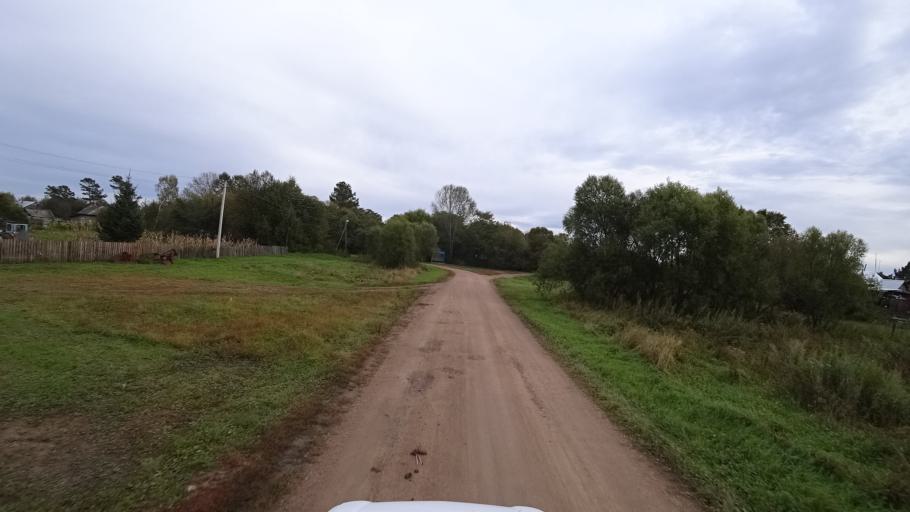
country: RU
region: Amur
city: Arkhara
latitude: 49.4354
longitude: 130.2651
